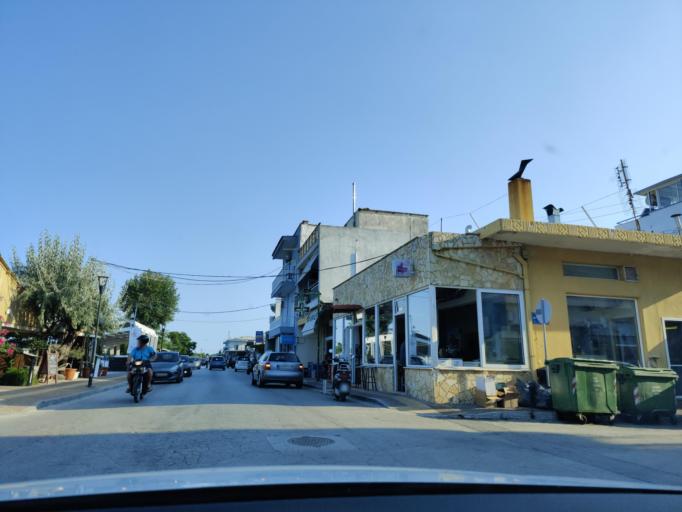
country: GR
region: East Macedonia and Thrace
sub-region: Nomos Kavalas
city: Nea Peramos
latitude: 40.8387
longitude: 24.3051
